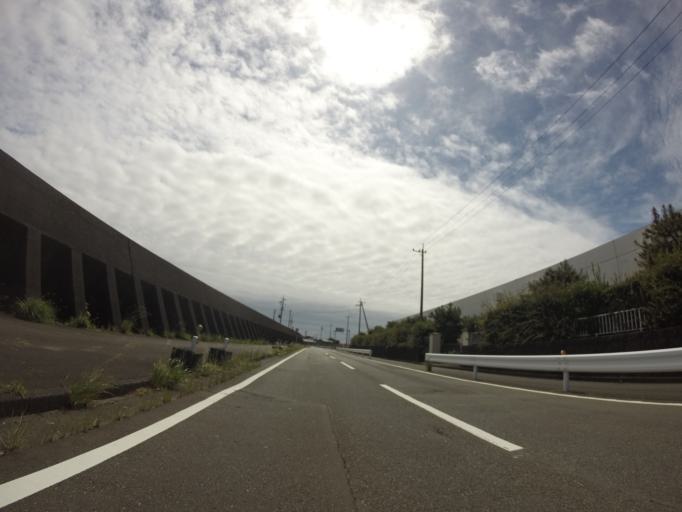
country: JP
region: Shizuoka
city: Yaizu
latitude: 34.8526
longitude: 138.3242
